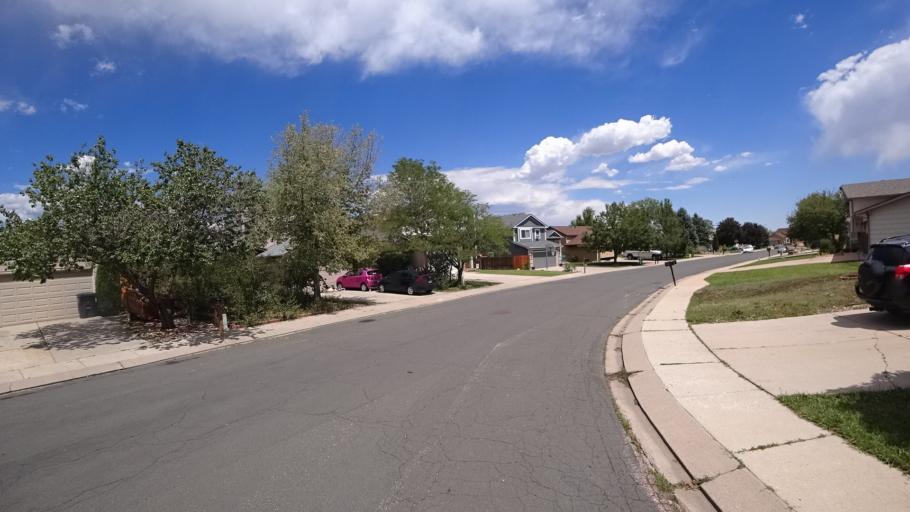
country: US
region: Colorado
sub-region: El Paso County
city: Stratmoor
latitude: 38.7860
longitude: -104.8006
